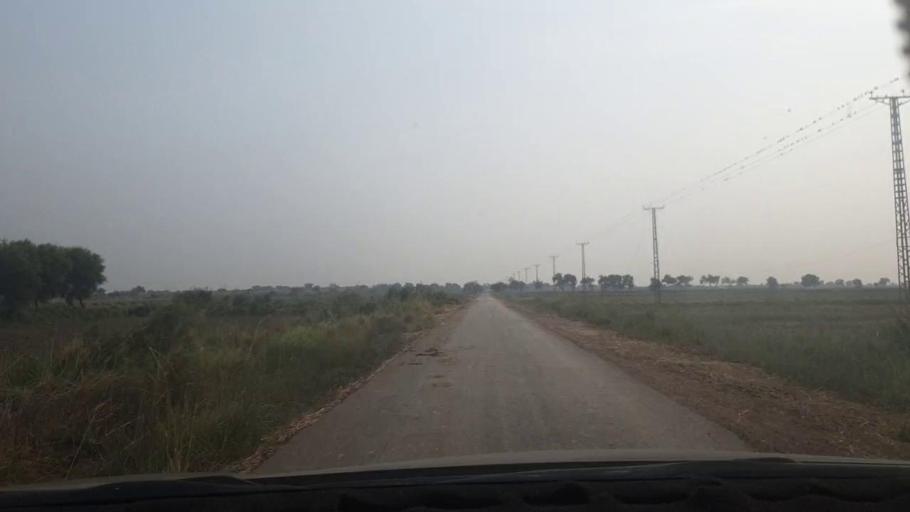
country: PK
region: Sindh
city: Jamshoro
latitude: 25.5145
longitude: 68.3145
